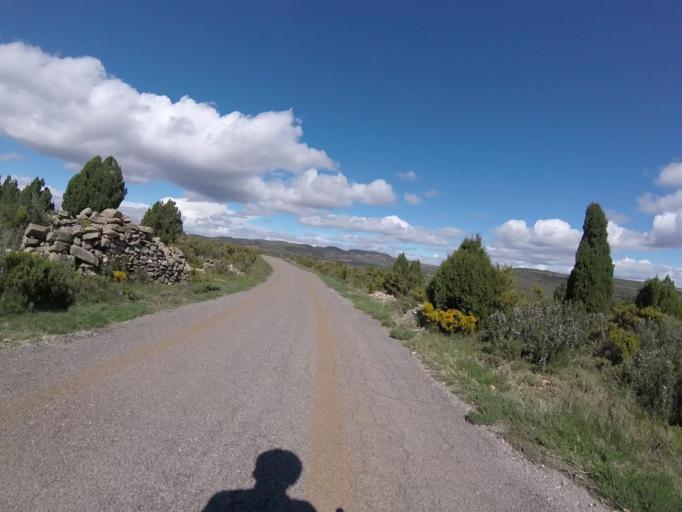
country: ES
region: Valencia
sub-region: Provincia de Castello
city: Culla
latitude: 40.3053
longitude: -0.1156
